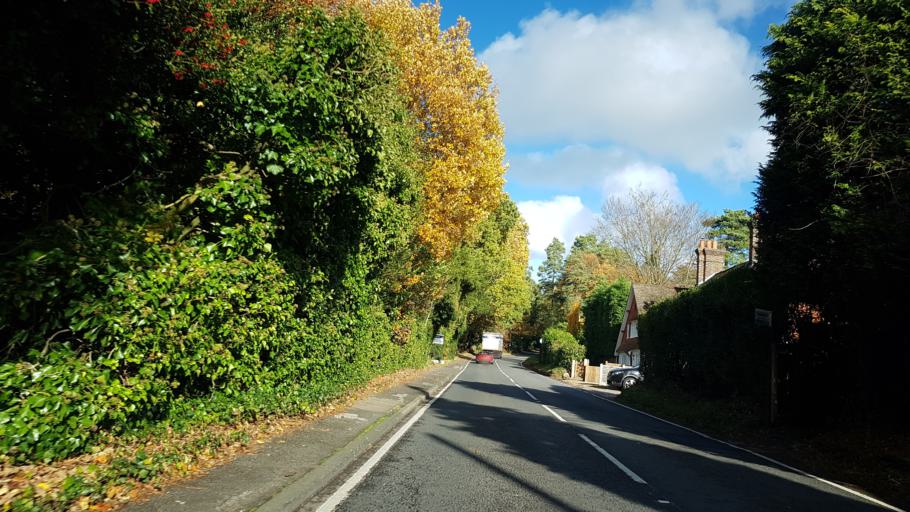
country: GB
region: England
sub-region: Surrey
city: Hindhead
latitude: 51.1065
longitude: -0.7333
